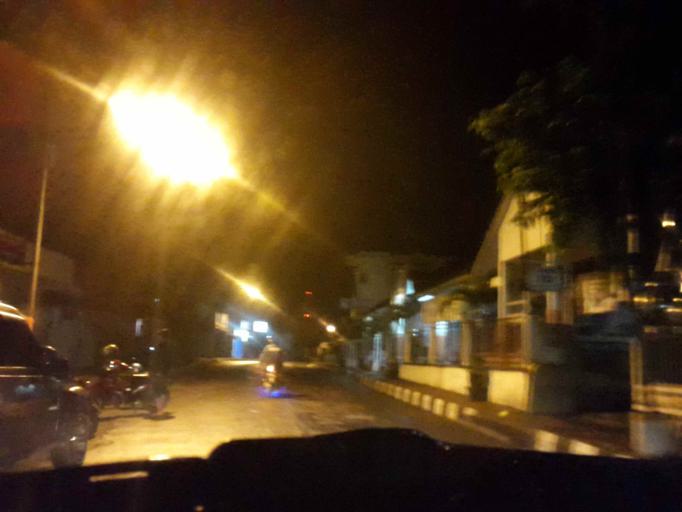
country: ID
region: Central Java
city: Wonosobo
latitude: -7.3623
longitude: 109.8982
